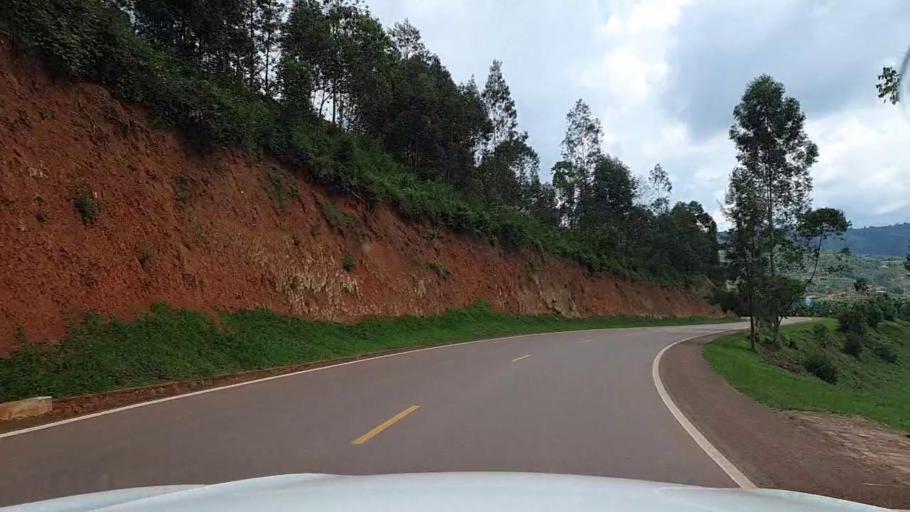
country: RW
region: Kigali
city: Kigali
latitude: -1.8112
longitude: 30.1213
